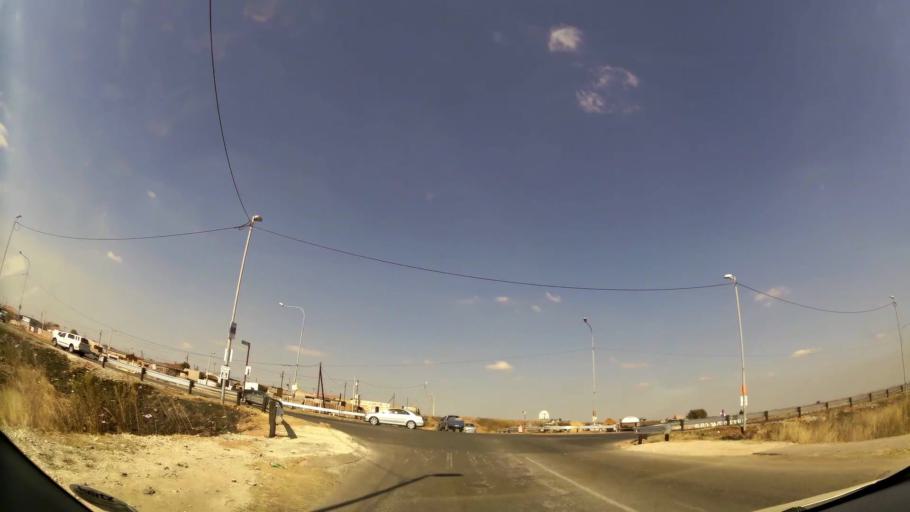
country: ZA
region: Gauteng
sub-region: West Rand District Municipality
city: Randfontein
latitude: -26.1739
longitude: 27.7782
